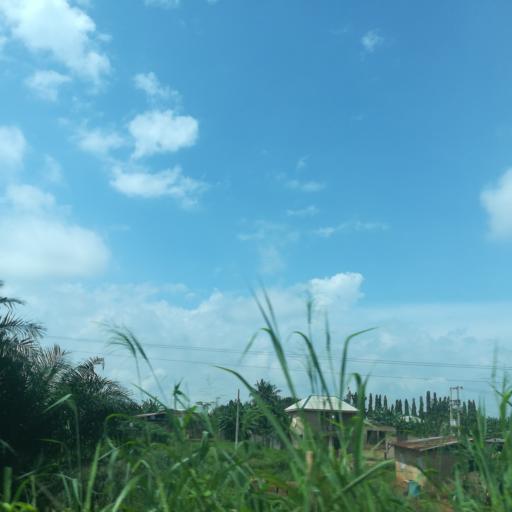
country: NG
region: Lagos
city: Ikorodu
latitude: 6.6613
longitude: 3.6796
